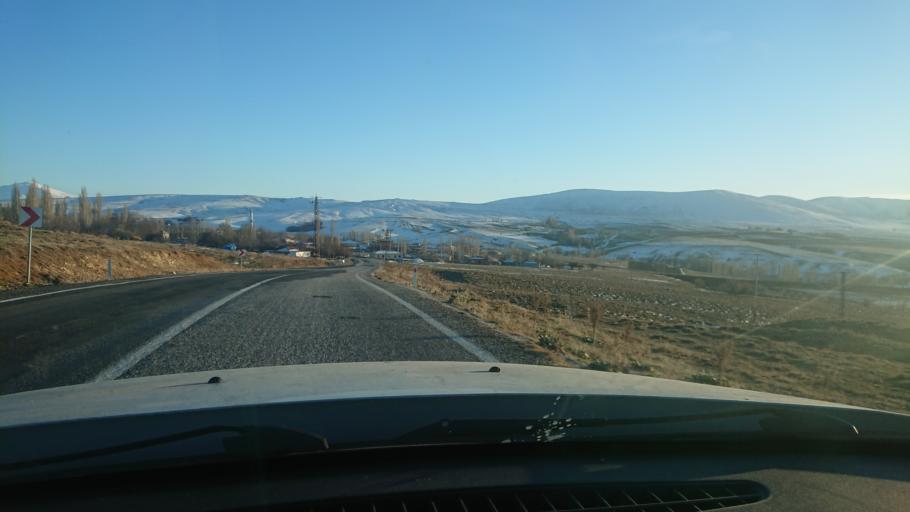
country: TR
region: Aksaray
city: Ortakoy
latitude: 38.7602
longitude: 33.9333
